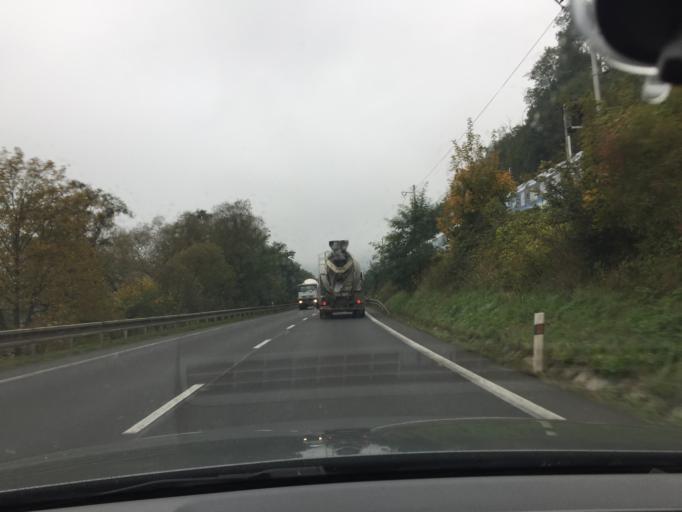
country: CZ
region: Ustecky
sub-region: Okres Usti nad Labem
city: Usti nad Labem
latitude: 50.6029
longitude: 14.0712
